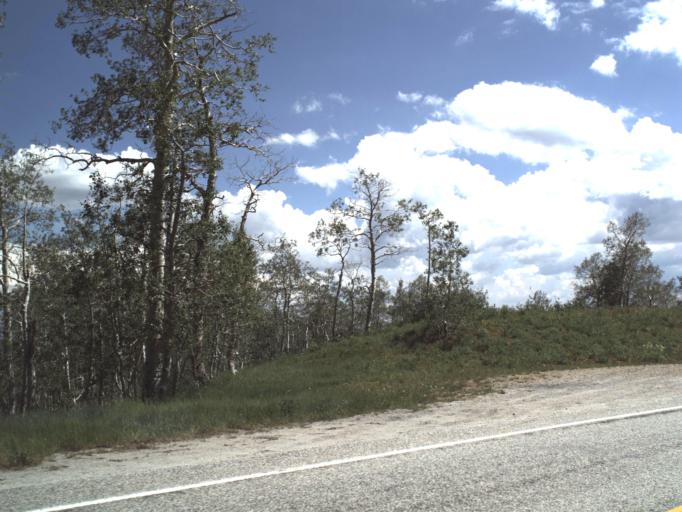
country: US
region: Utah
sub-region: Weber County
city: Wolf Creek
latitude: 41.4091
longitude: -111.5247
